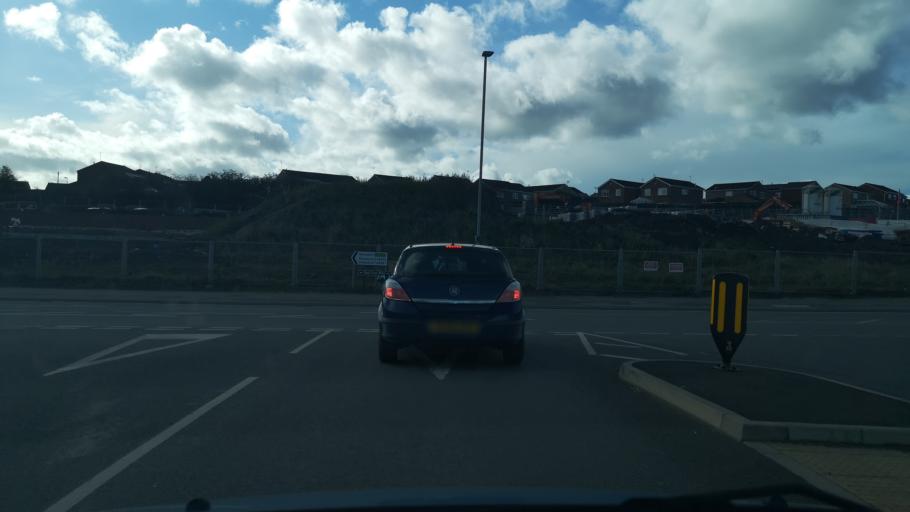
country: GB
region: England
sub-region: City and Borough of Wakefield
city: Wakefield
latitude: 53.6955
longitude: -1.4738
